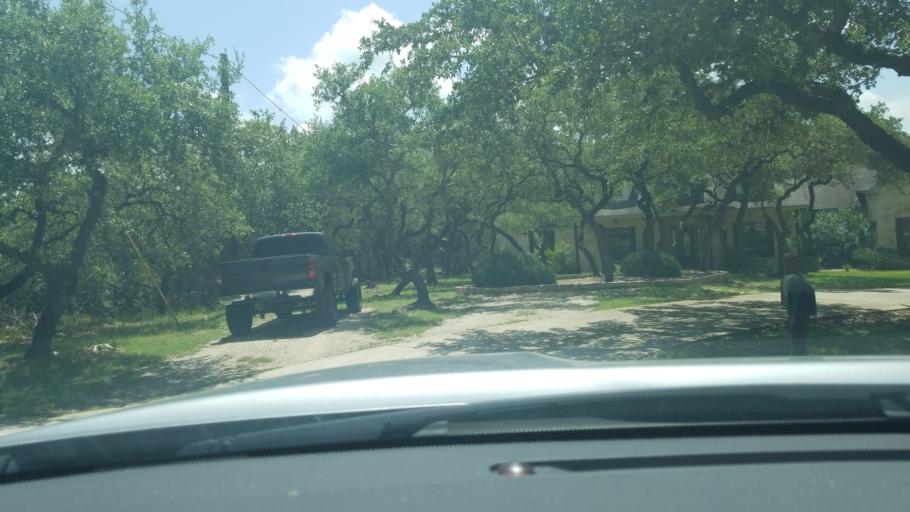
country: US
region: Texas
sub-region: Bexar County
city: Timberwood Park
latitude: 29.6891
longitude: -98.4824
